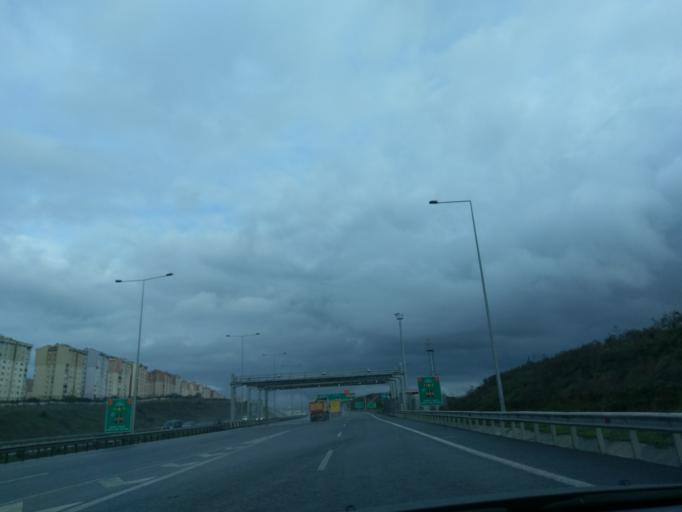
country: TR
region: Istanbul
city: Basaksehir
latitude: 41.0859
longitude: 28.8137
